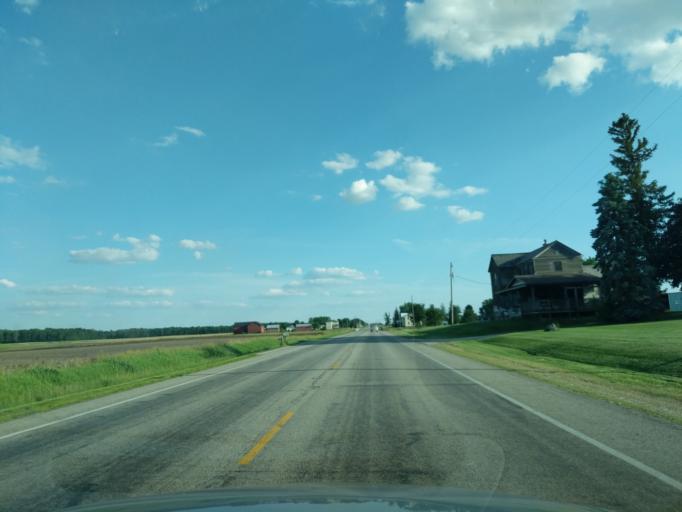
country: US
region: Indiana
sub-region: Whitley County
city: Columbia City
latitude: 41.0581
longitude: -85.4705
